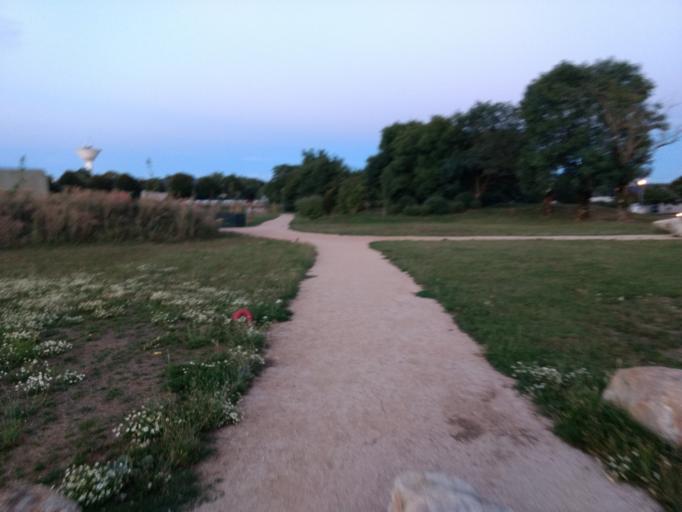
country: FR
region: Midi-Pyrenees
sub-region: Departement de l'Aveyron
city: Olemps
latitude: 44.3391
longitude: 2.5526
